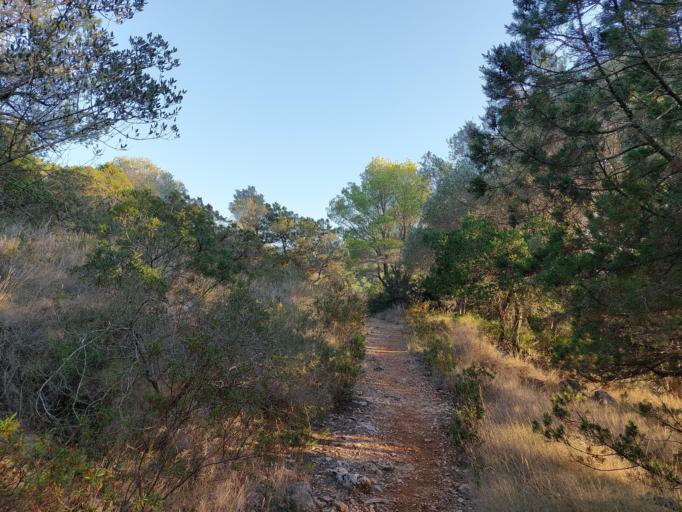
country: HR
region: Dubrovacko-Neretvanska
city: Smokvica
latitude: 42.7713
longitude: 16.7886
